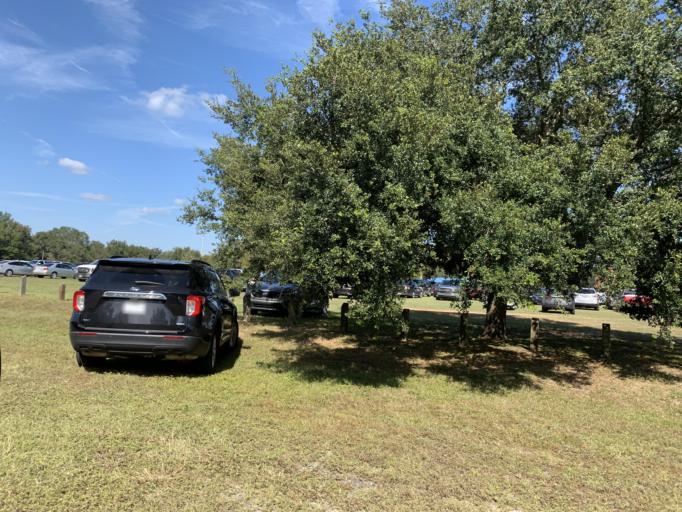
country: US
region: Florida
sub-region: Marion County
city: Ocala
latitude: 29.1643
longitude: -82.0893
